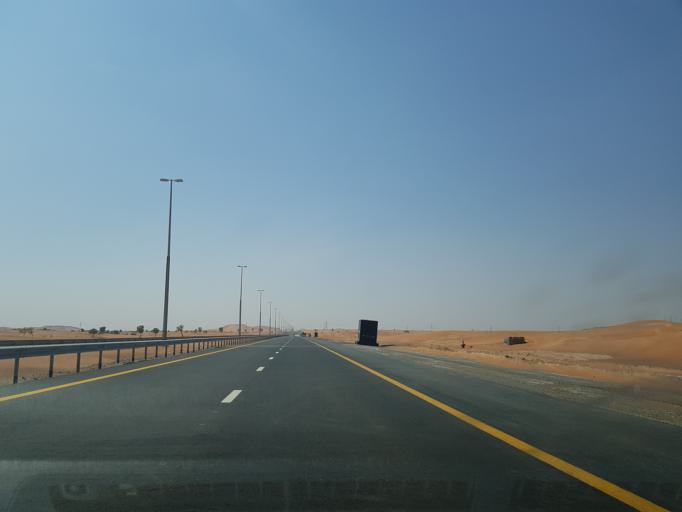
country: AE
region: Ash Shariqah
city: Adh Dhayd
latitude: 25.2417
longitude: 55.8764
